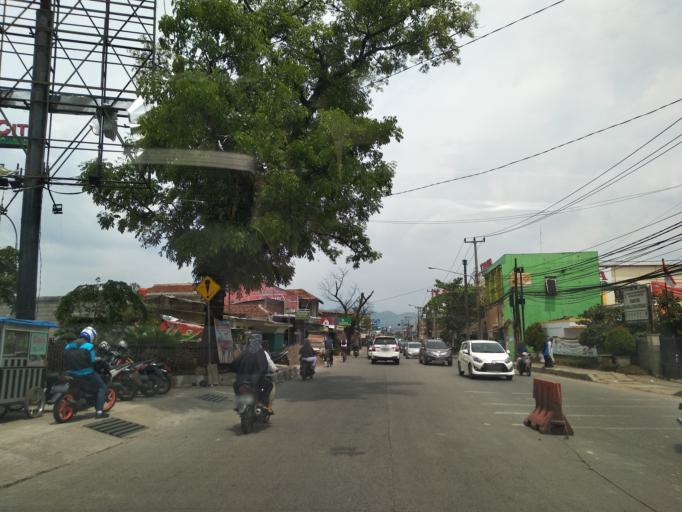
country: ID
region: West Java
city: Pameungpeuk
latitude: -6.9670
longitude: 107.6376
